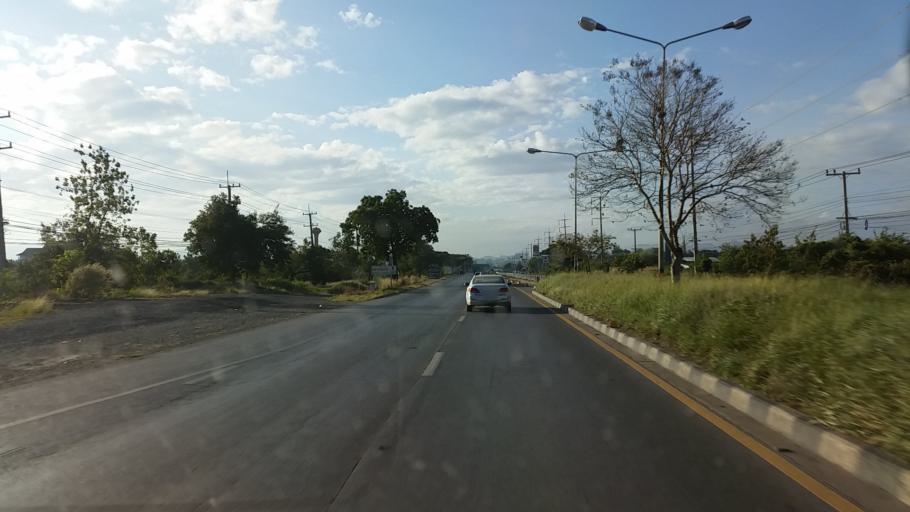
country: TH
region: Lop Buri
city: Phatthana Nikhom
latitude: 14.8552
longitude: 100.9096
